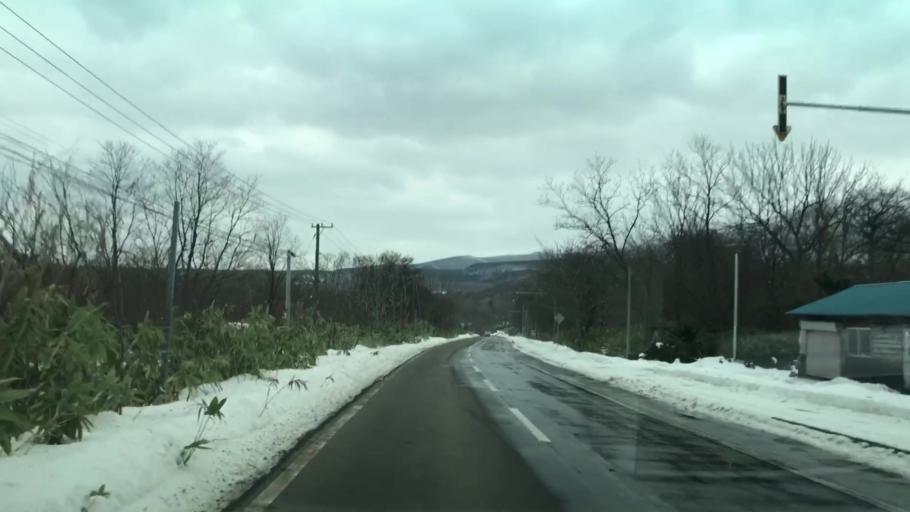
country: JP
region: Hokkaido
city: Yoichi
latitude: 43.3356
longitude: 140.4646
